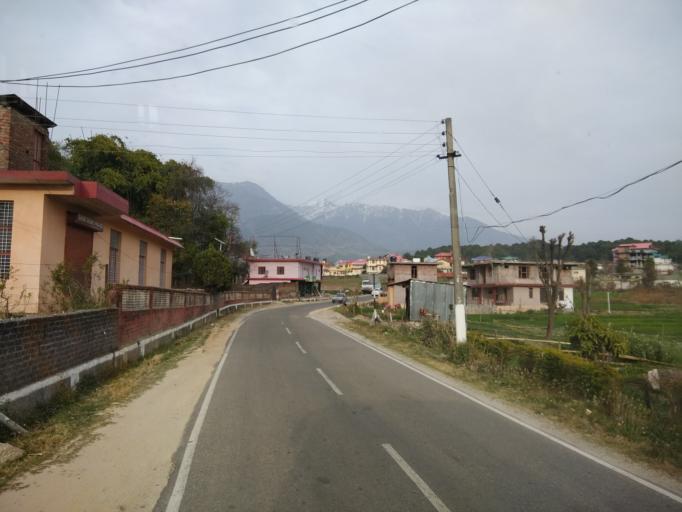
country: IN
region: Himachal Pradesh
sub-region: Kangra
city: Palampur
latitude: 32.1111
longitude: 76.4991
